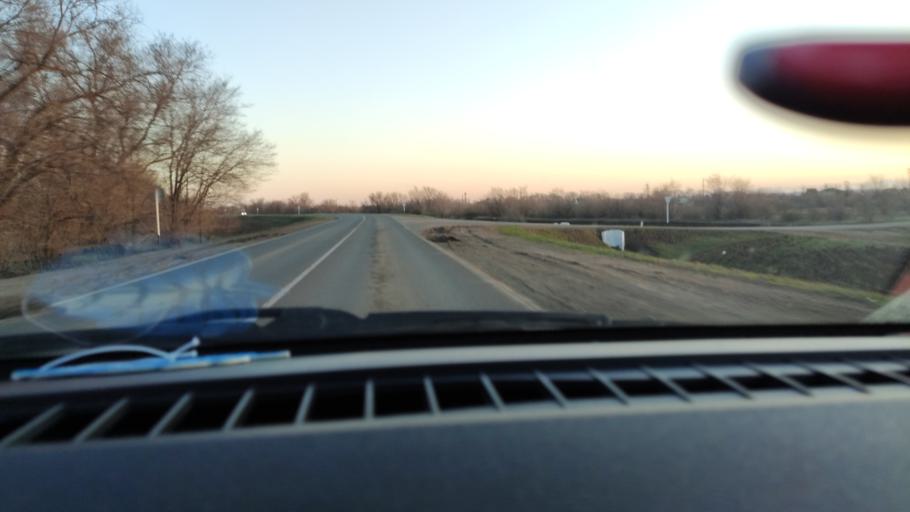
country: RU
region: Saratov
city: Privolzhskiy
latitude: 51.3385
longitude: 46.0405
